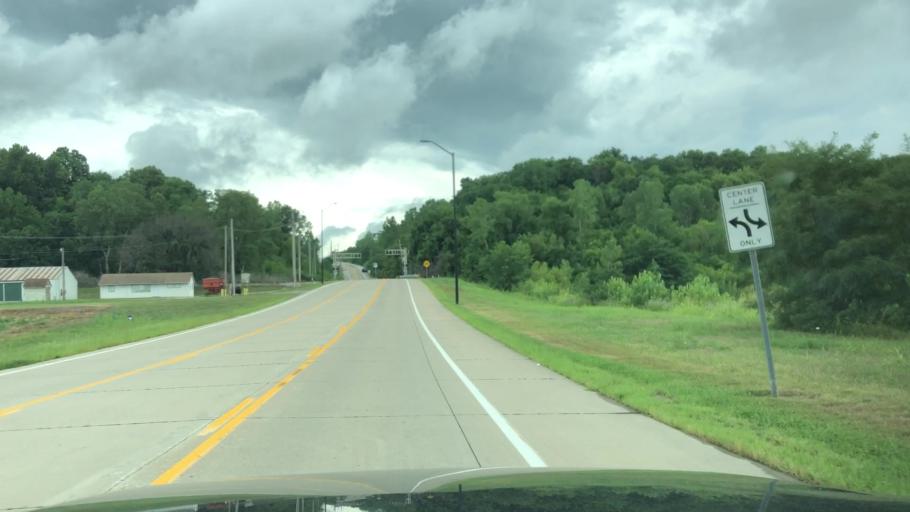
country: US
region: Missouri
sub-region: Saint Charles County
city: Saint Peters
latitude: 38.8059
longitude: -90.5809
